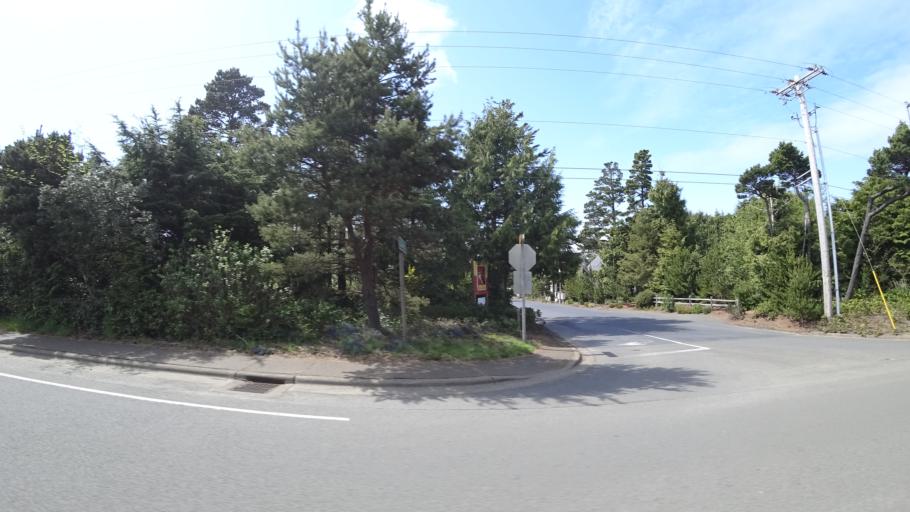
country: US
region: Oregon
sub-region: Lincoln County
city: Lincoln Beach
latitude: 44.8619
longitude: -124.0377
